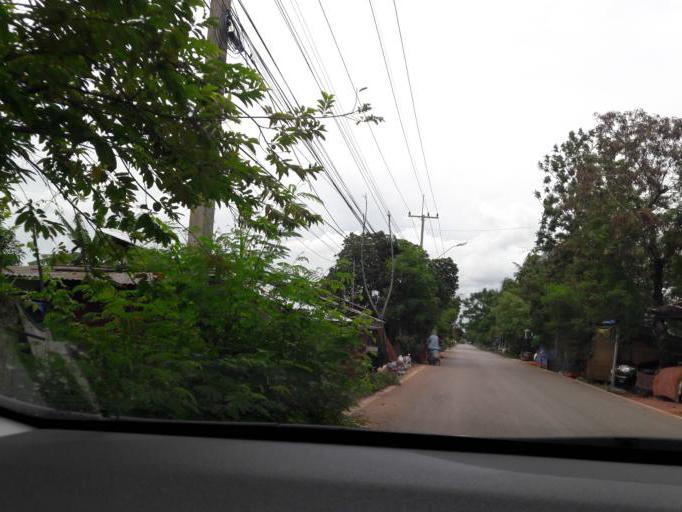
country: TH
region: Samut Sakhon
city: Ban Phaeo
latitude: 13.5494
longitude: 100.0454
